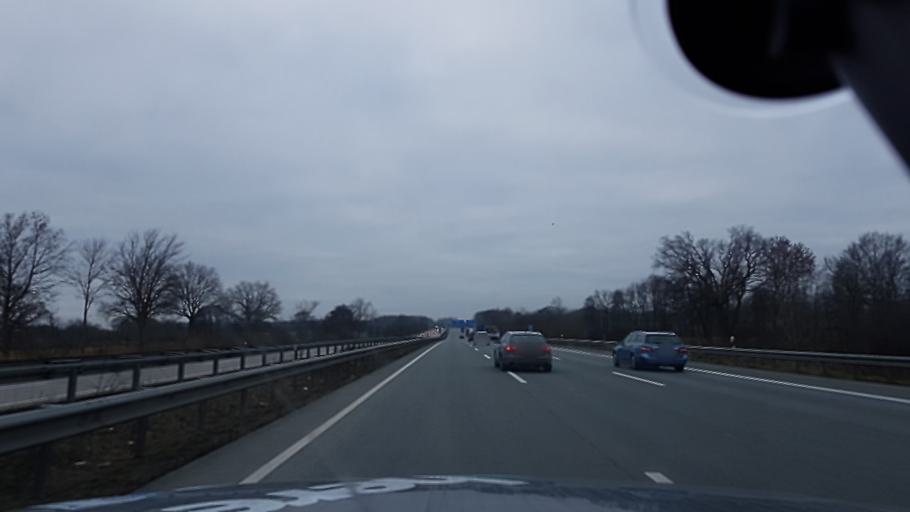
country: DE
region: Schleswig-Holstein
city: Lasbek
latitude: 53.7264
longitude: 10.3453
